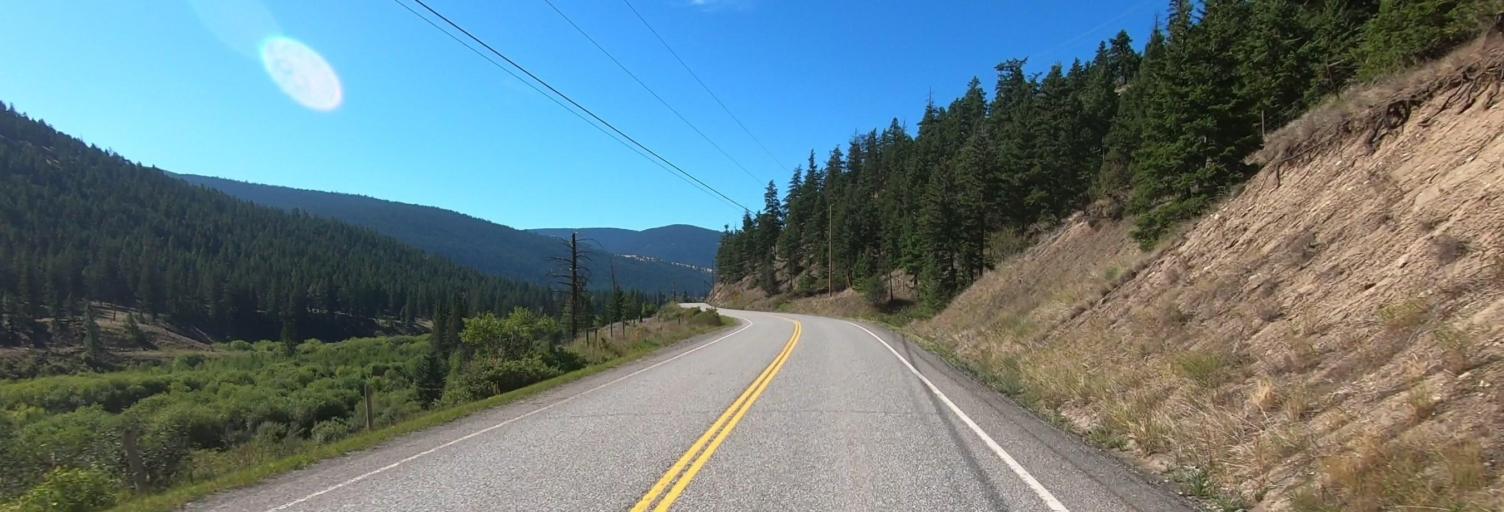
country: CA
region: British Columbia
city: Cache Creek
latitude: 50.8597
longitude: -121.5305
